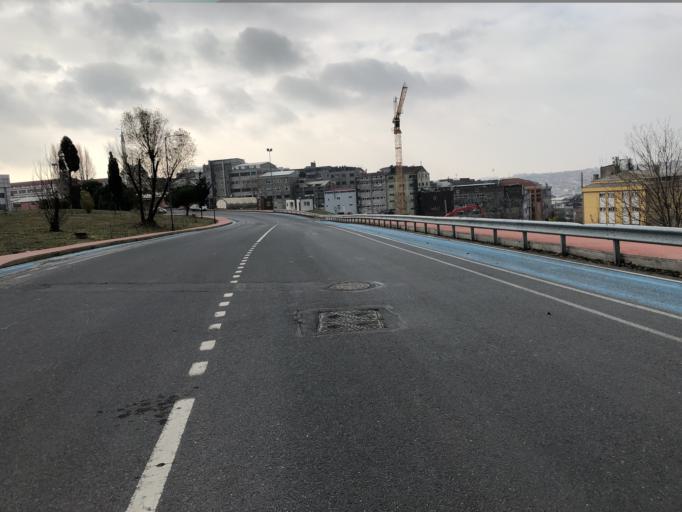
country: TR
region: Istanbul
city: merter keresteciler
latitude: 41.0236
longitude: 28.8863
